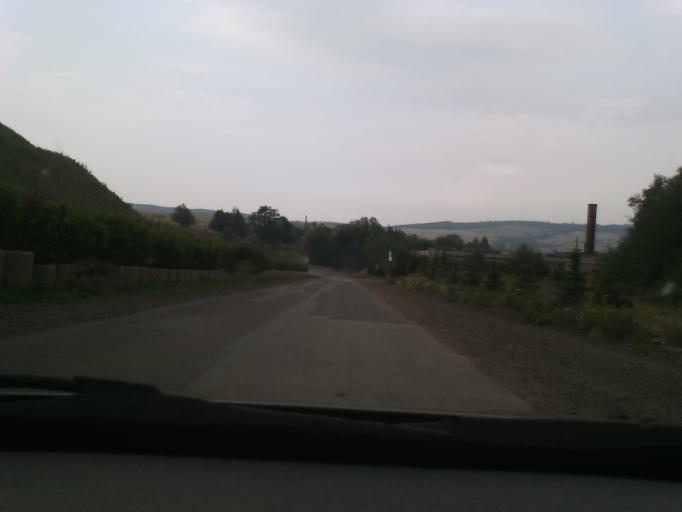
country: CZ
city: Mezimesti
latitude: 50.6925
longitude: 16.2712
